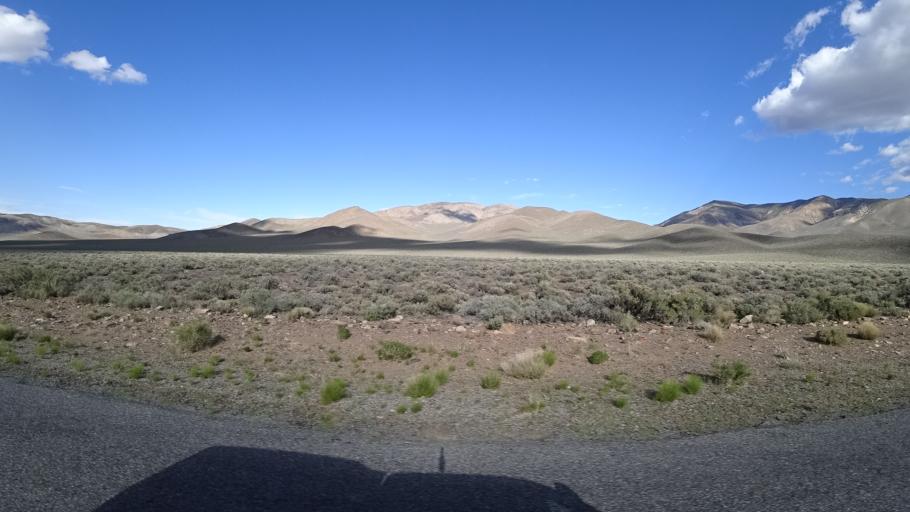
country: US
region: California
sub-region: San Bernardino County
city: Searles Valley
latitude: 36.3414
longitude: -117.1355
